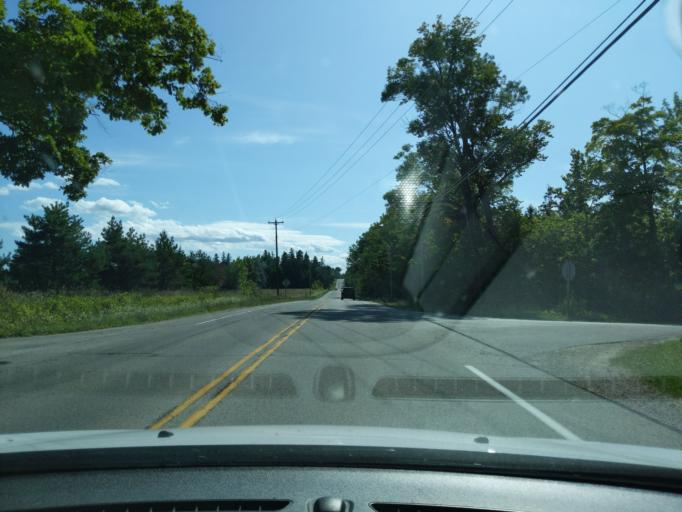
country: US
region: Wisconsin
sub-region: Door County
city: Sturgeon Bay
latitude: 45.2222
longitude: -87.1061
